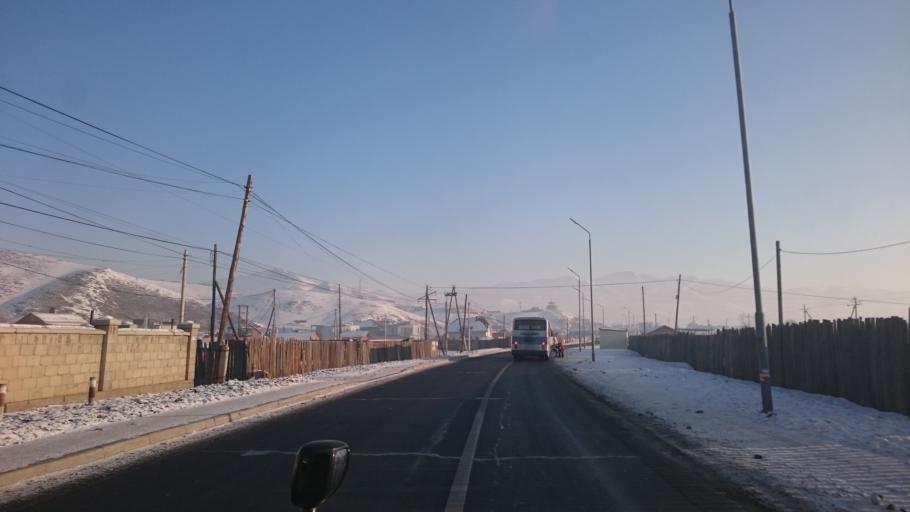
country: MN
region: Ulaanbaatar
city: Ulaanbaatar
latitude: 47.9231
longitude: 107.1315
